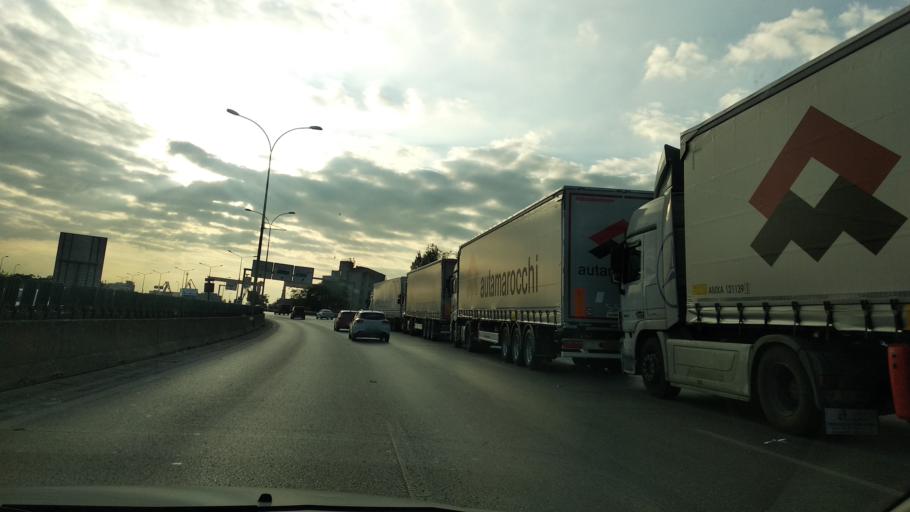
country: TR
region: Istanbul
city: Pendik
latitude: 40.8692
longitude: 29.2765
